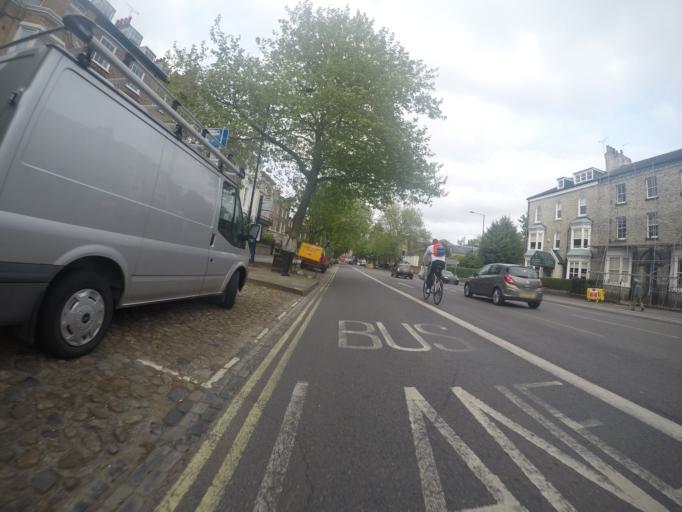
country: GB
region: England
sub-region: City of York
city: York
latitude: 53.9526
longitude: -1.0960
